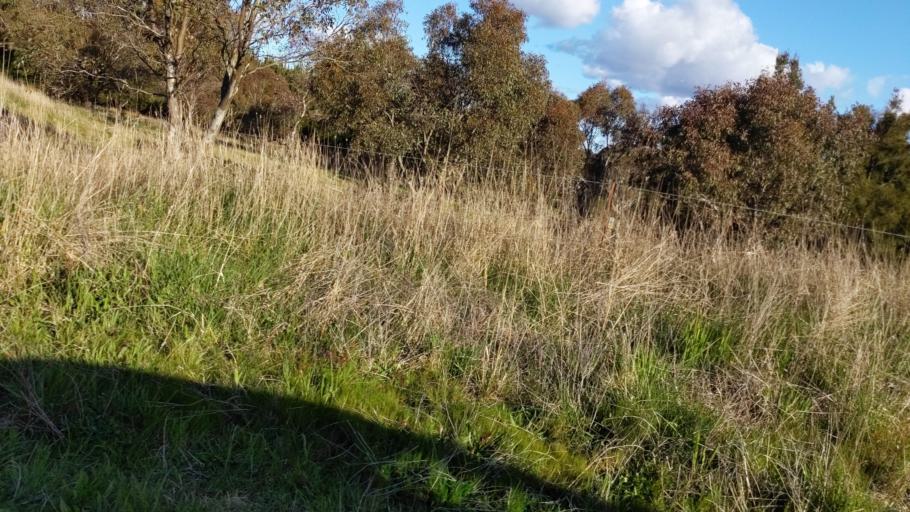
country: AU
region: New South Wales
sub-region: Blayney
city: Millthorpe
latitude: -33.4014
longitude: 149.3136
